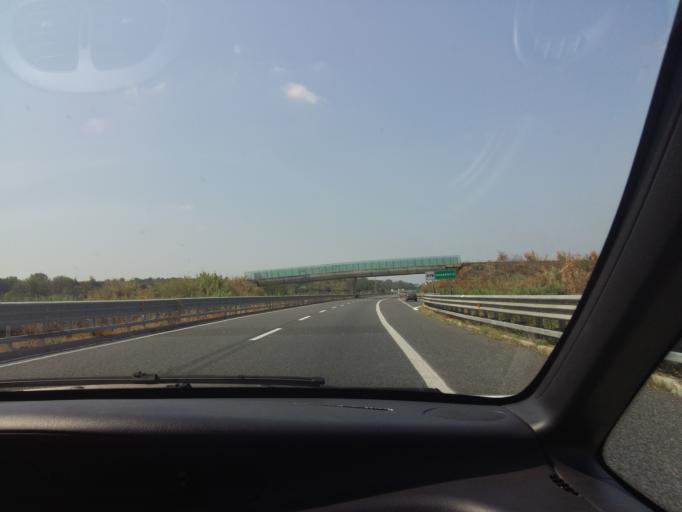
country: IT
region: Calabria
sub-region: Provincia di Reggio Calabria
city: Rosarno
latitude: 38.5008
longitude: 16.0291
